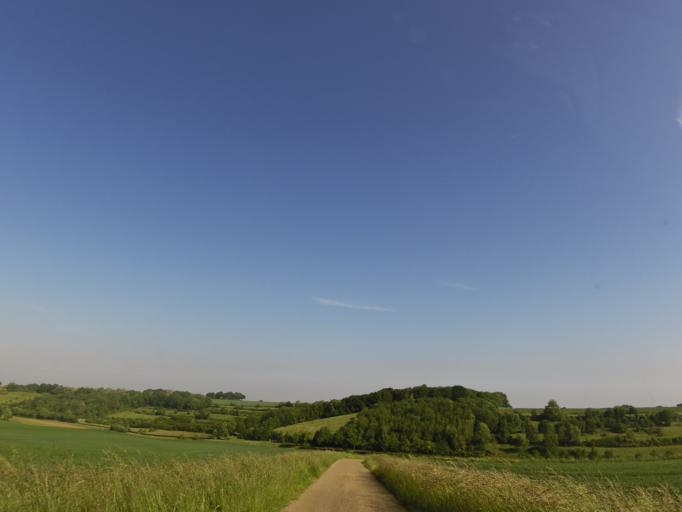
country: NL
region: Limburg
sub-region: Gemeente Voerendaal
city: Ubachsberg
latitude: 50.8457
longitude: 5.9270
